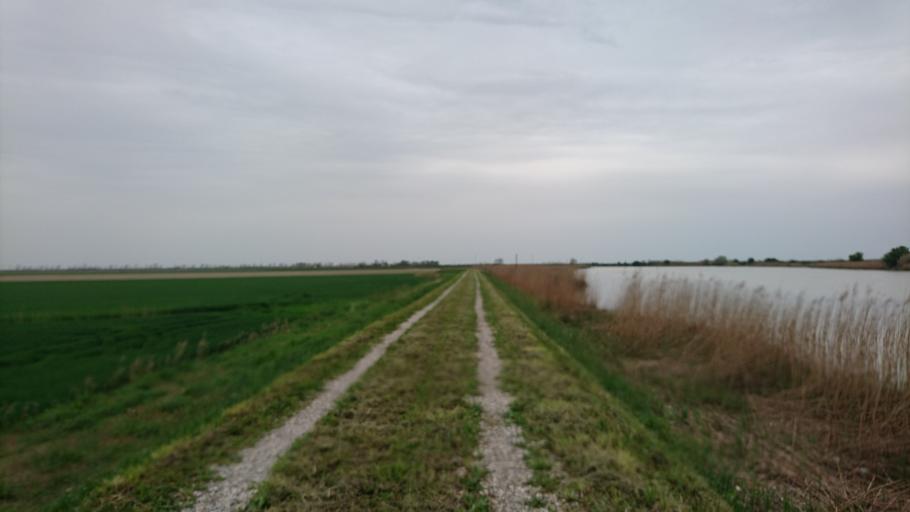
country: IT
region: Veneto
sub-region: Provincia di Venezia
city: Lugugnana
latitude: 45.6793
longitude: 12.9529
